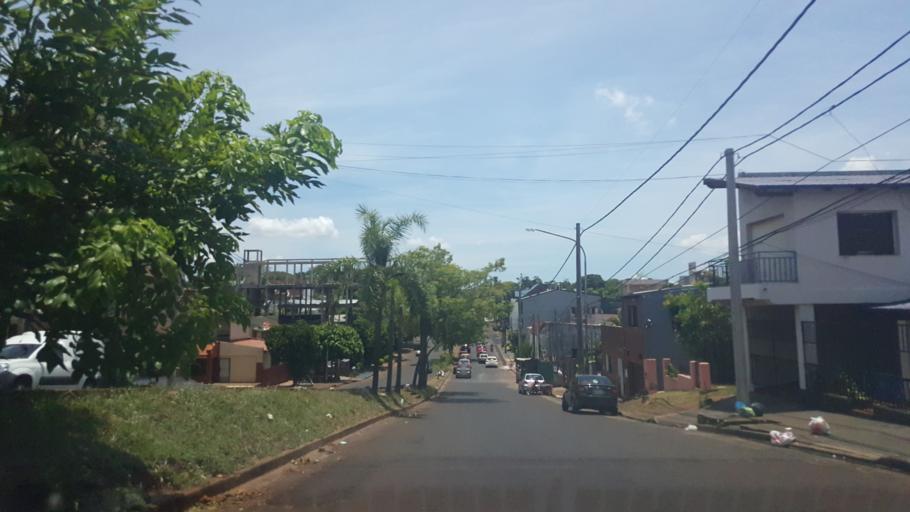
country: AR
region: Misiones
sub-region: Departamento de Capital
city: Posadas
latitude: -27.3636
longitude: -55.9031
